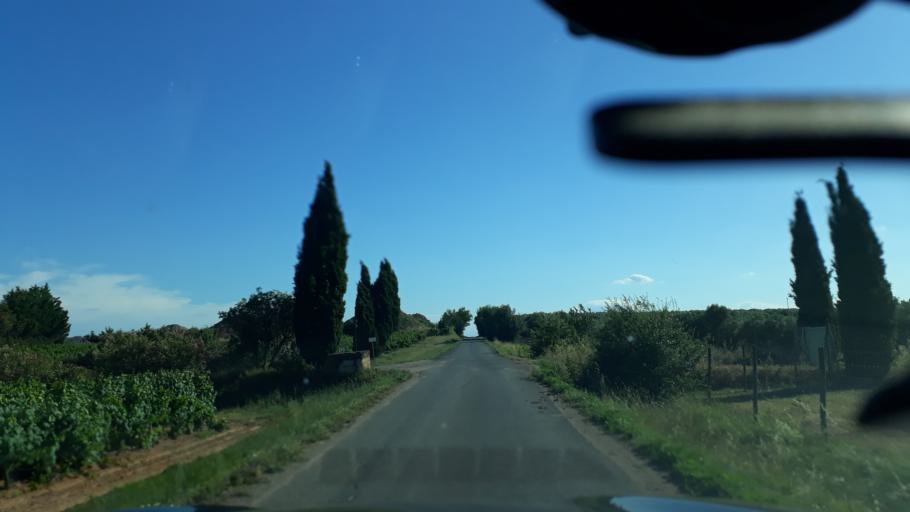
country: FR
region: Languedoc-Roussillon
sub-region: Departement de l'Herault
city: Marseillan
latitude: 43.3348
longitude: 3.5046
